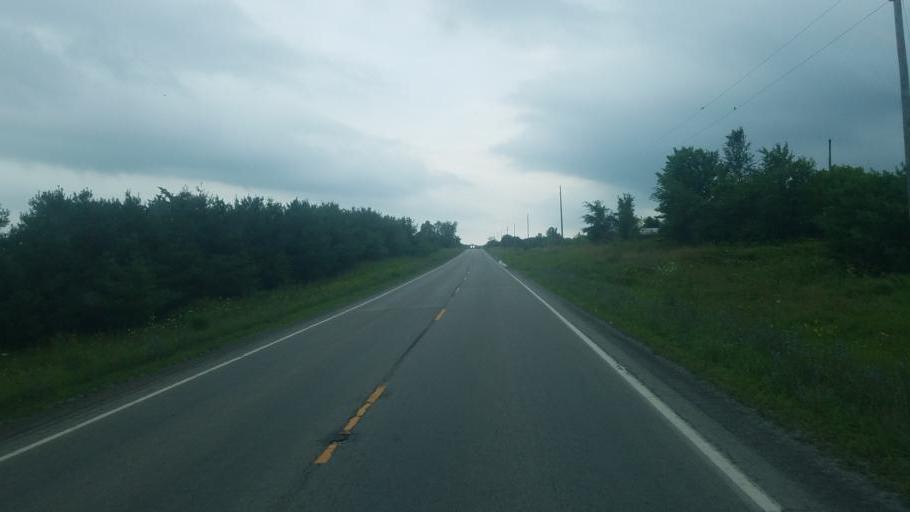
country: US
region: Ohio
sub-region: Logan County
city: Russells Point
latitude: 40.5784
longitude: -83.8395
